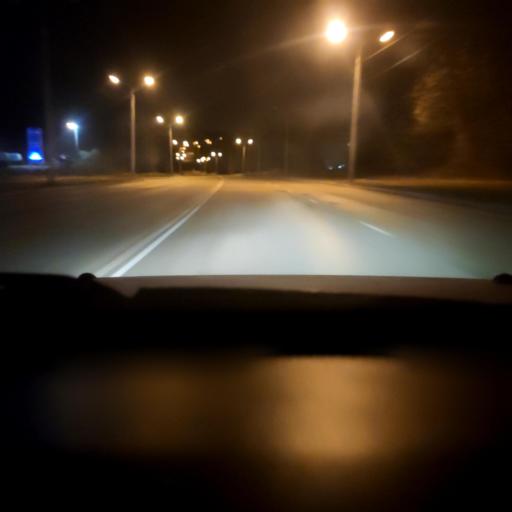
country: RU
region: Perm
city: Perm
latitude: 58.0664
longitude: 56.3656
